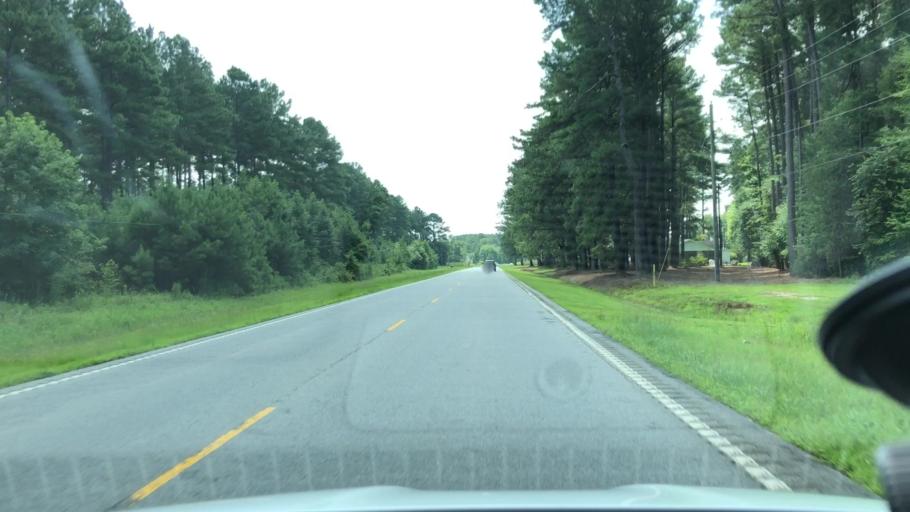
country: US
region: North Carolina
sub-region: Beaufort County
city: Washington
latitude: 35.6689
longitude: -77.0757
